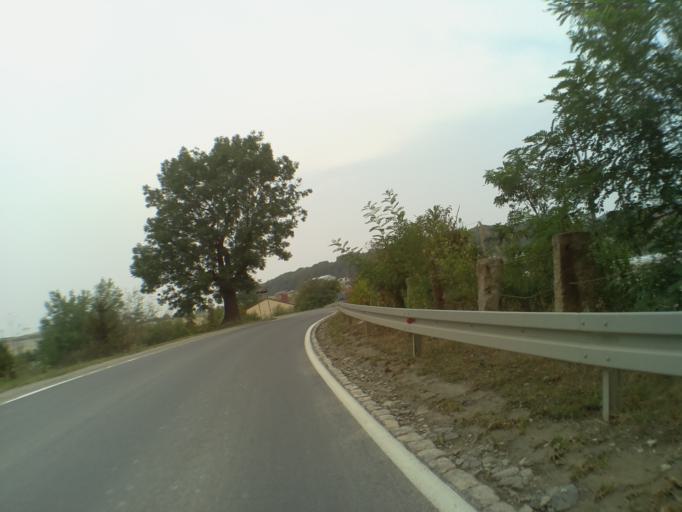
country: PL
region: Lower Silesian Voivodeship
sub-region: Powiat swidnicki
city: Strzegom
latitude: 50.9639
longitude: 16.3376
